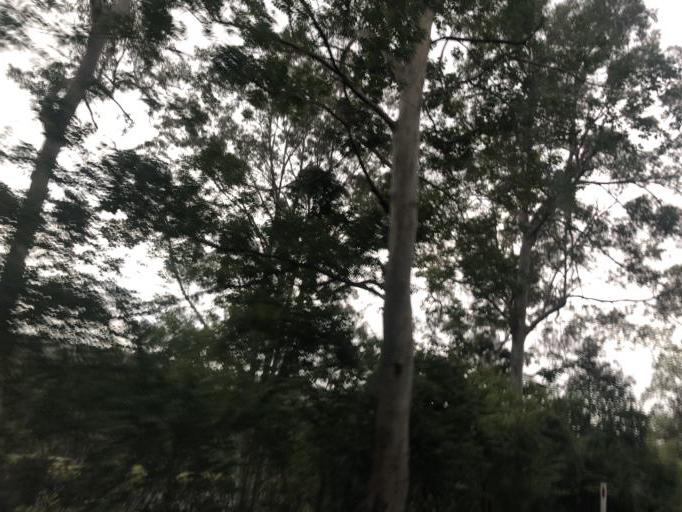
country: AU
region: New South Wales
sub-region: Coffs Harbour
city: Boambee
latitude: -30.2641
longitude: 153.0101
